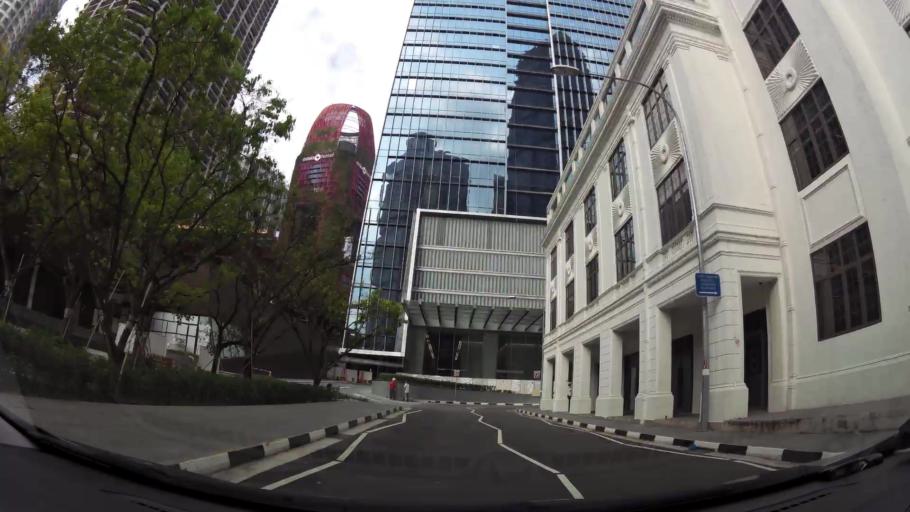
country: SG
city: Singapore
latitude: 1.2769
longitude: 103.8466
